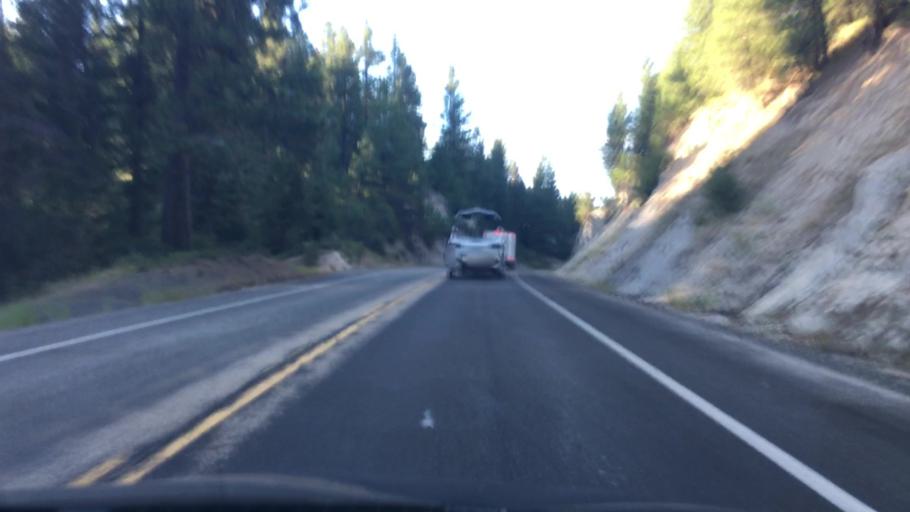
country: US
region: Idaho
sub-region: Valley County
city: Cascade
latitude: 44.5648
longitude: -116.0301
